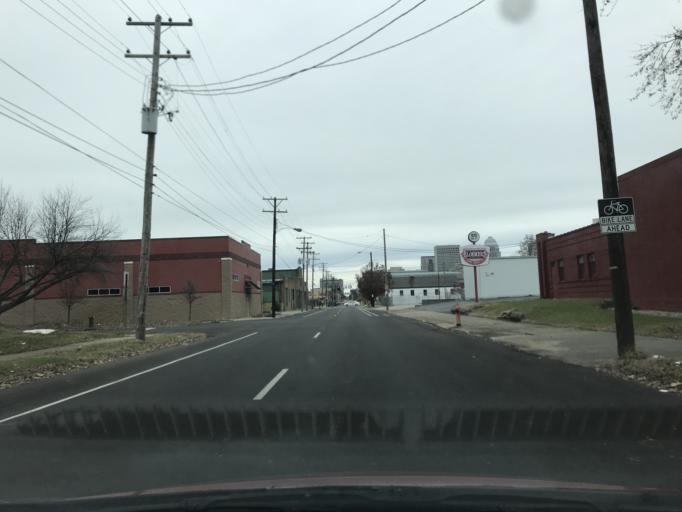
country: US
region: Kentucky
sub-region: Jefferson County
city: Louisville
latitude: 38.2414
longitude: -85.7643
